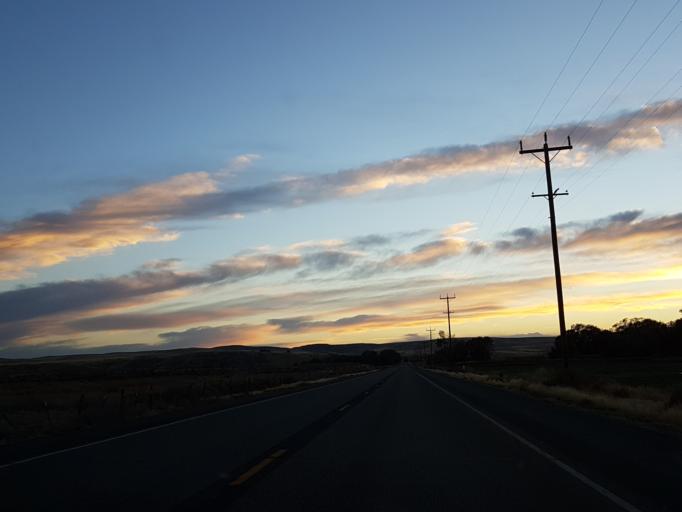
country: US
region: Oregon
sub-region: Malheur County
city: Vale
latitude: 43.9344
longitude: -117.3825
